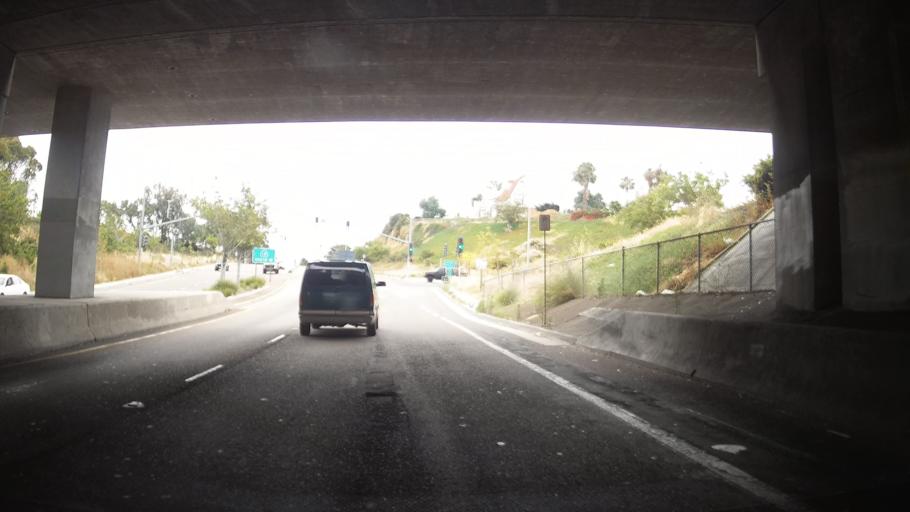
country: US
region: California
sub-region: San Diego County
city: San Diego
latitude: 32.7133
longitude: -117.1195
